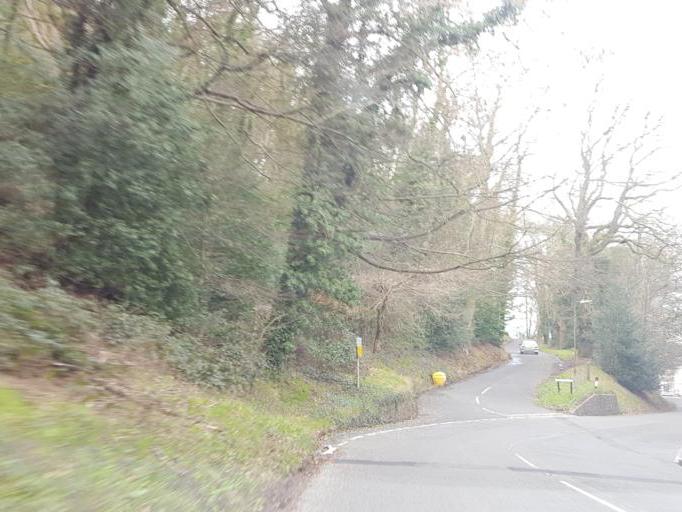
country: GB
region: England
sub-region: Worcestershire
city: Great Malvern
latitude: 52.1037
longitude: -2.3310
